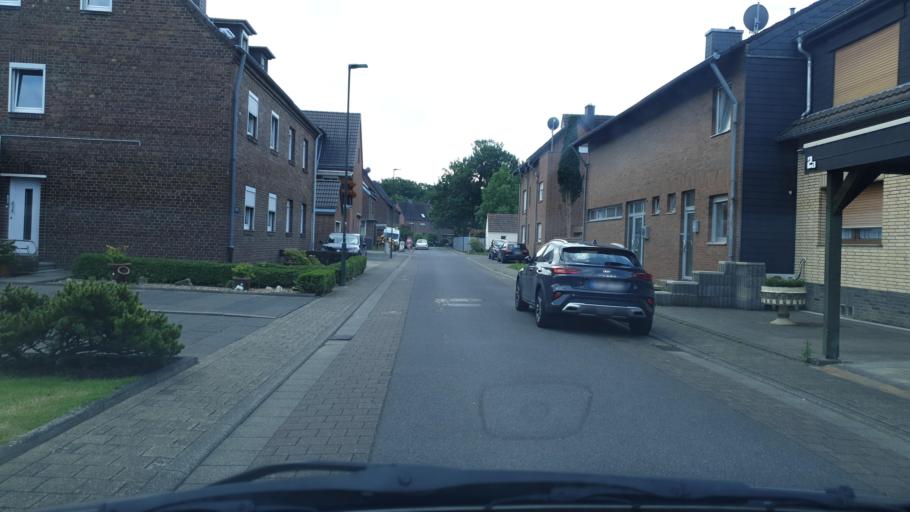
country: DE
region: North Rhine-Westphalia
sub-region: Regierungsbezirk Koln
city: Kerpen
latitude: 50.9171
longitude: 6.7277
